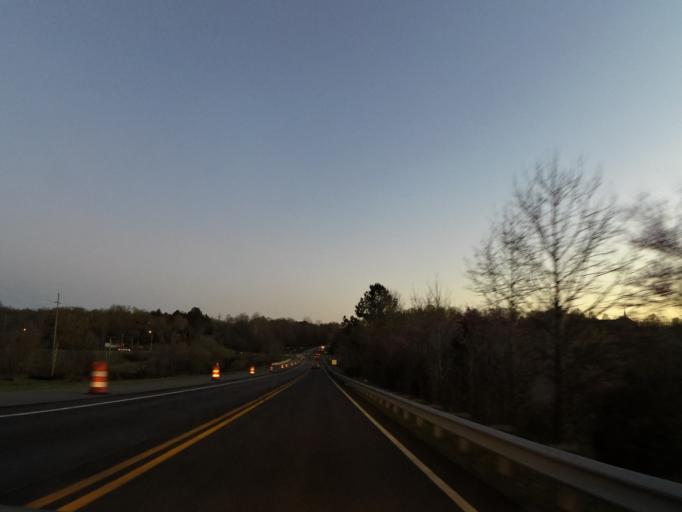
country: US
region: Tennessee
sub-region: Robertson County
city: Springfield
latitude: 36.4696
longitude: -86.8932
